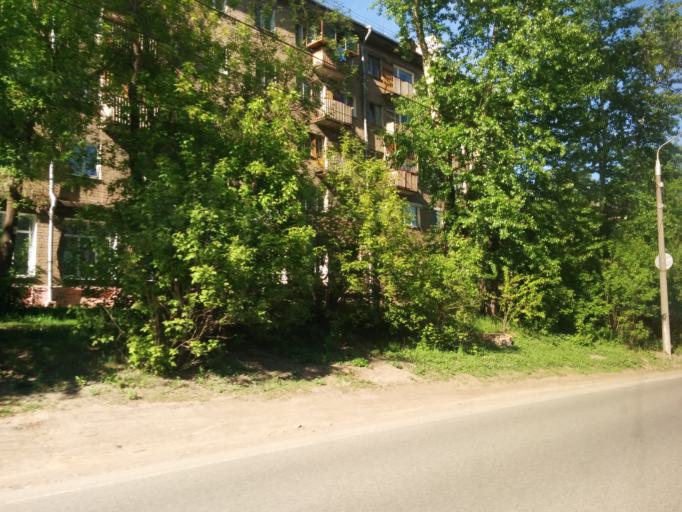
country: RU
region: Perm
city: Kondratovo
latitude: 58.0451
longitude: 56.0896
